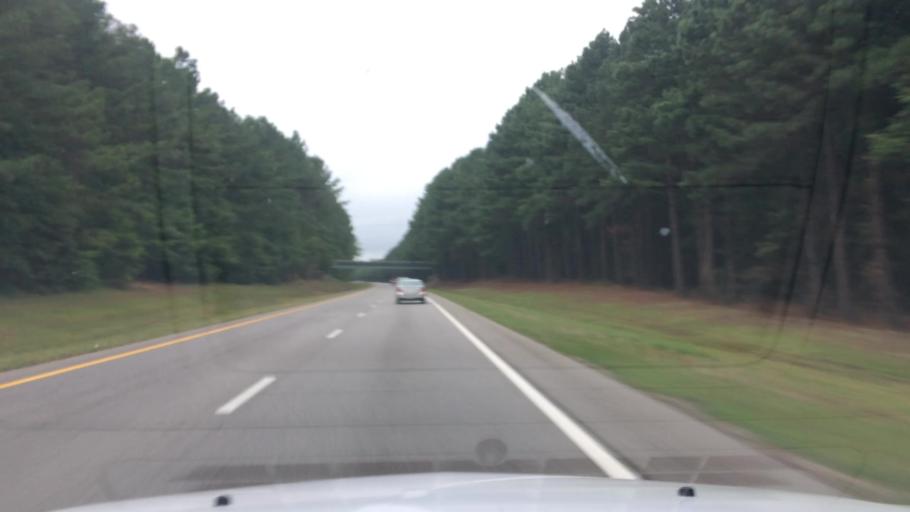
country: US
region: North Carolina
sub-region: Nash County
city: Spring Hope
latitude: 35.7930
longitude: -78.1502
